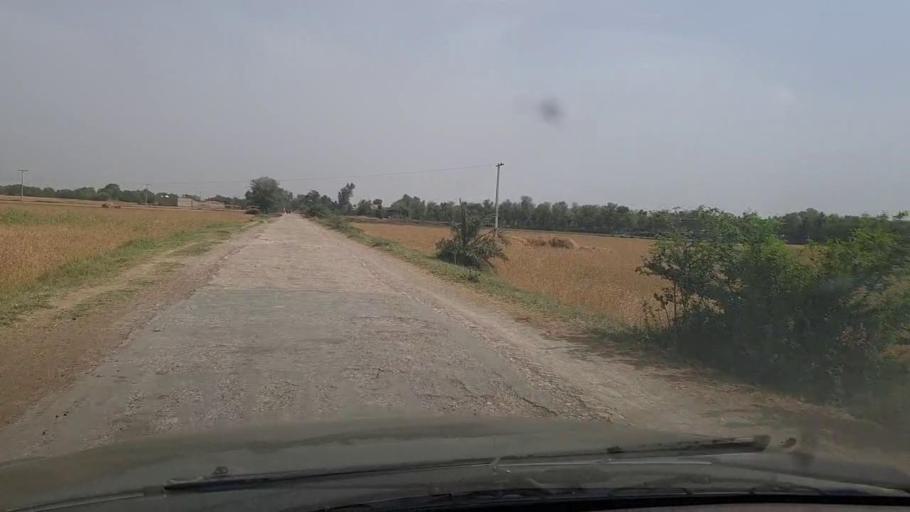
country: PK
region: Sindh
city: Lakhi
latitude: 27.8450
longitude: 68.7580
